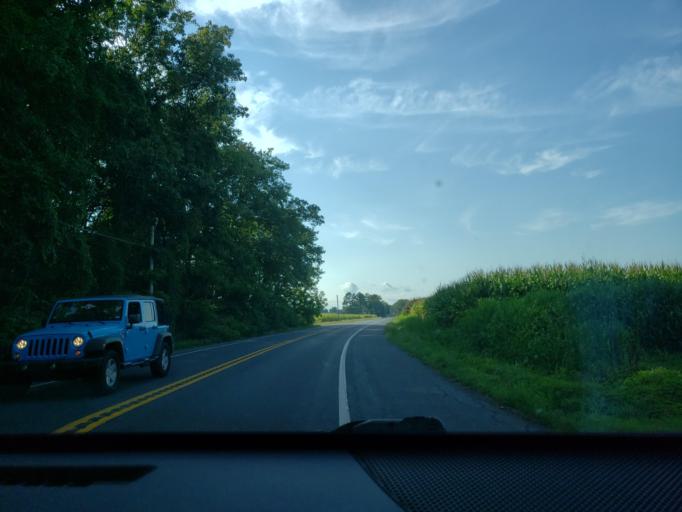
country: US
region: Delaware
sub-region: Sussex County
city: Milton
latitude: 38.7553
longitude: -75.2561
